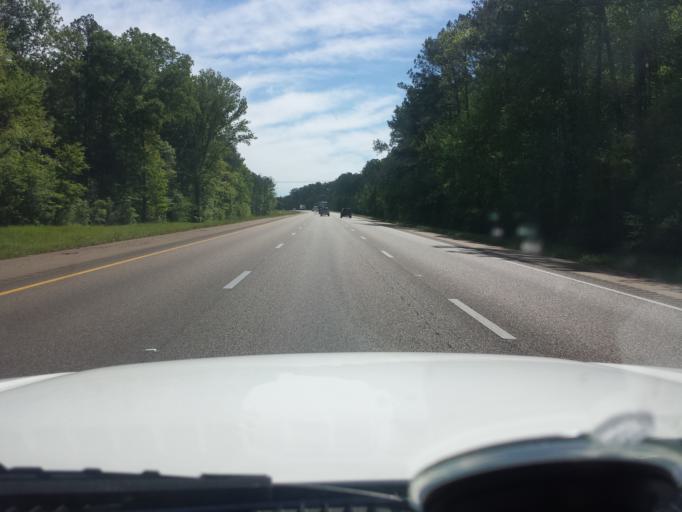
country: US
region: Mississippi
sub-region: Rankin County
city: Pearl
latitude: 32.2659
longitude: -90.1106
